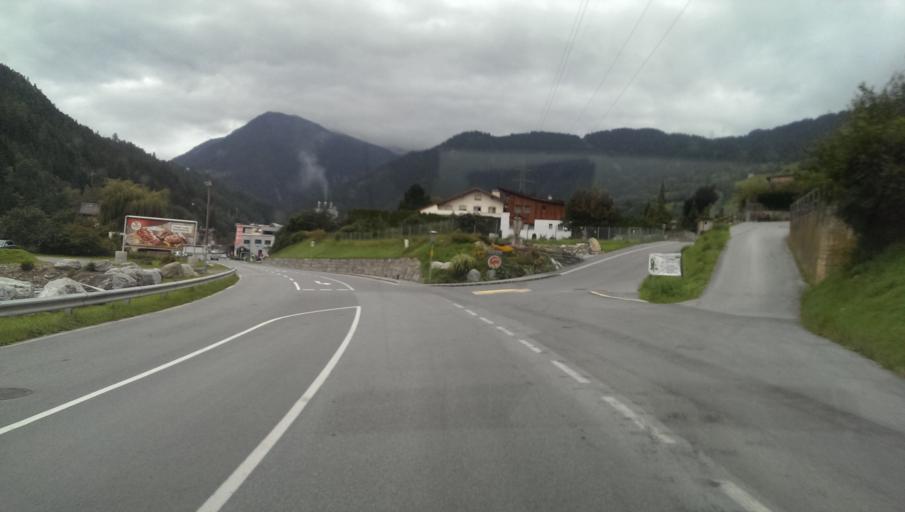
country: AT
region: Tyrol
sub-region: Politischer Bezirk Landeck
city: Grins
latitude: 47.1360
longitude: 10.5194
